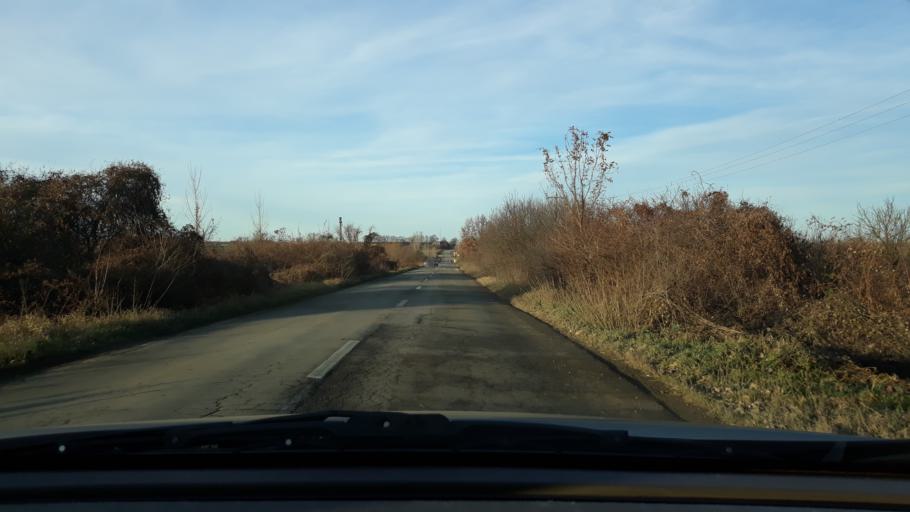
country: RO
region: Bihor
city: Foglas
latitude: 47.2422
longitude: 22.5349
